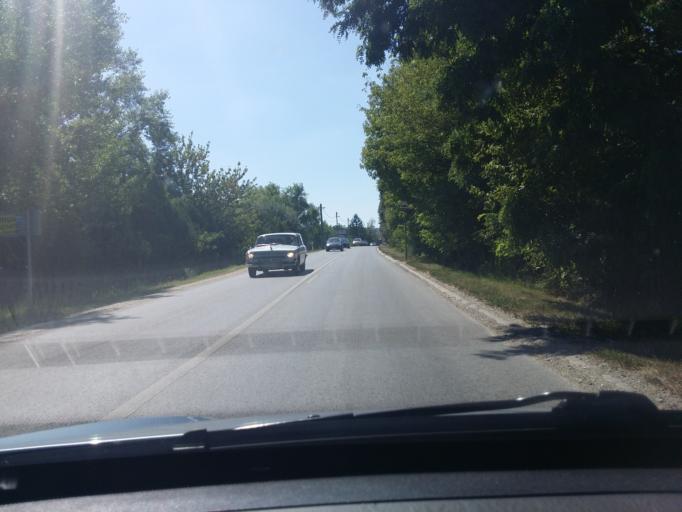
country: HU
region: Pest
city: Pomaz
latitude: 47.6457
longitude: 19.0446
